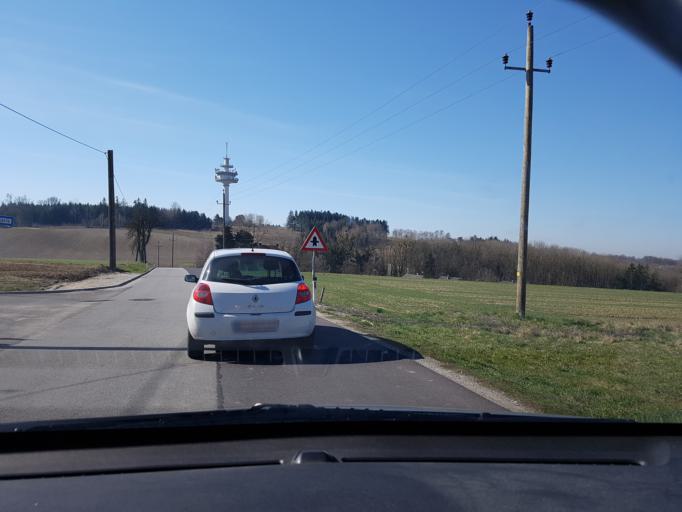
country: AT
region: Upper Austria
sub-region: Politischer Bezirk Linz-Land
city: Ansfelden
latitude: 48.2074
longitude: 14.2969
